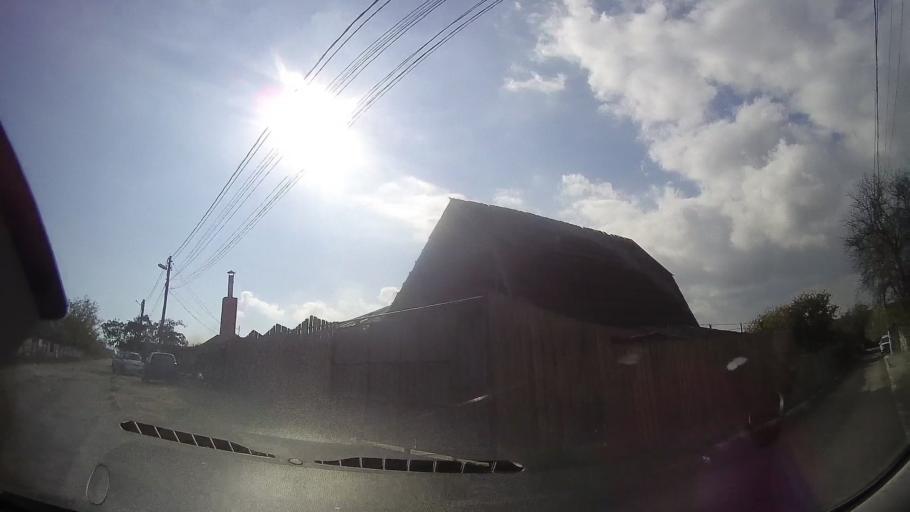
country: RO
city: Eforie Sud
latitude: 44.0131
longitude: 28.6448
